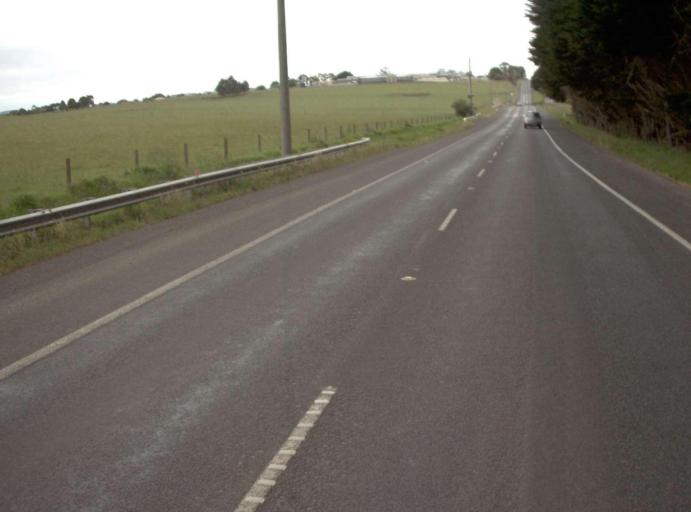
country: AU
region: Victoria
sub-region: Baw Baw
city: Warragul
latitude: -38.4953
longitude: 145.9520
